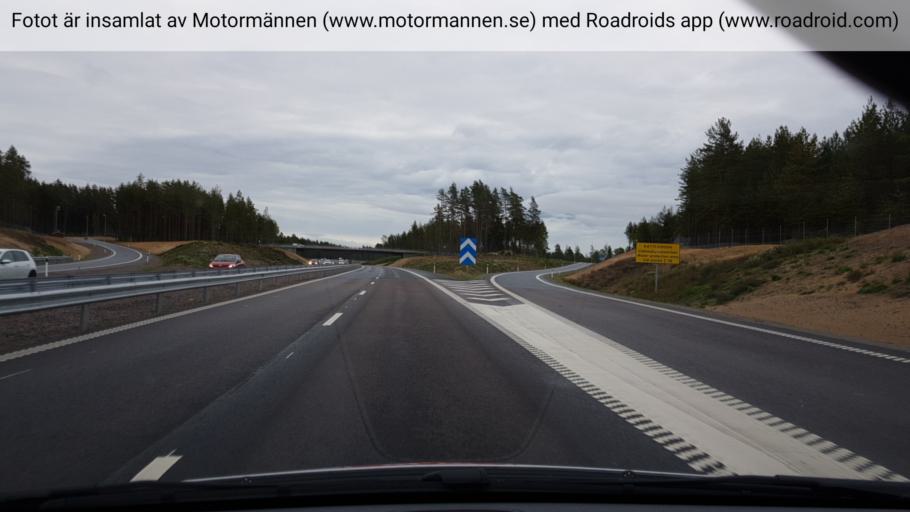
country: SE
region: Vaermland
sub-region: Kils Kommun
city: Kil
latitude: 59.3843
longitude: 13.3295
